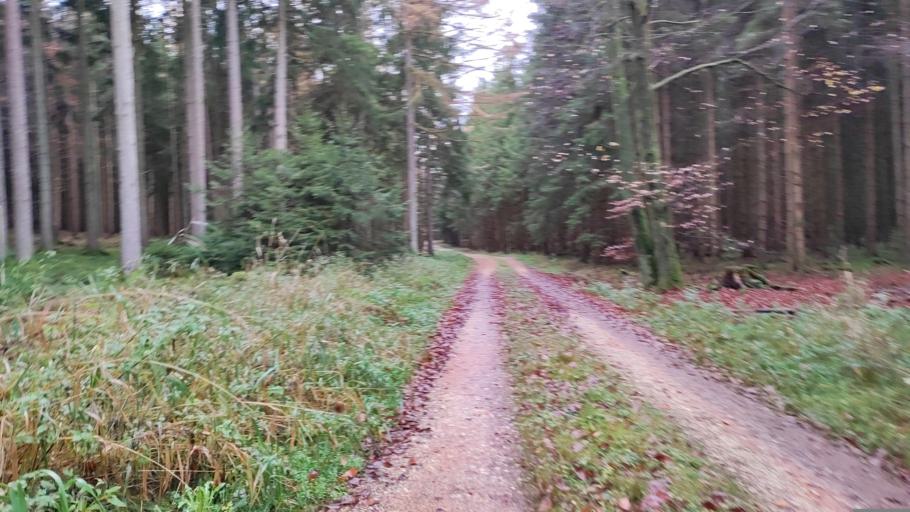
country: DE
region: Bavaria
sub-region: Swabia
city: Burtenbach
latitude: 48.3371
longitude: 10.5000
